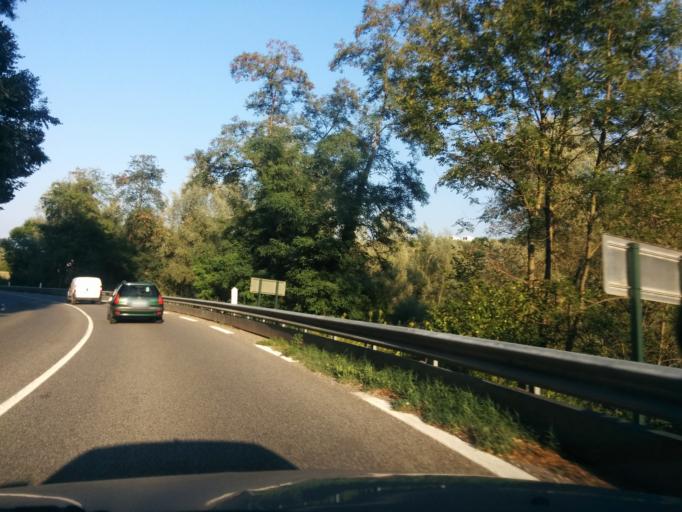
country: FR
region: Rhone-Alpes
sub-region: Departement de l'Isere
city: Les Abrets
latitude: 45.5313
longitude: 5.6235
